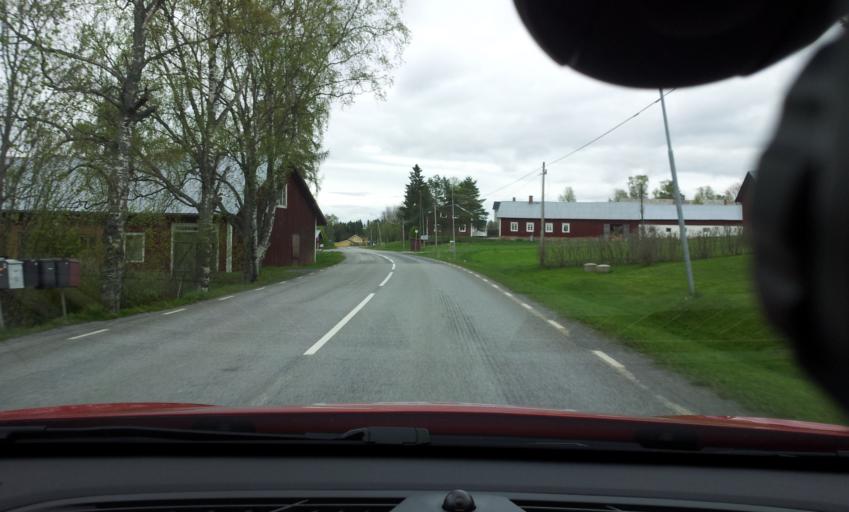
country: SE
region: Jaemtland
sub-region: OEstersunds Kommun
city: Ostersund
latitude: 63.1250
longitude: 14.6924
